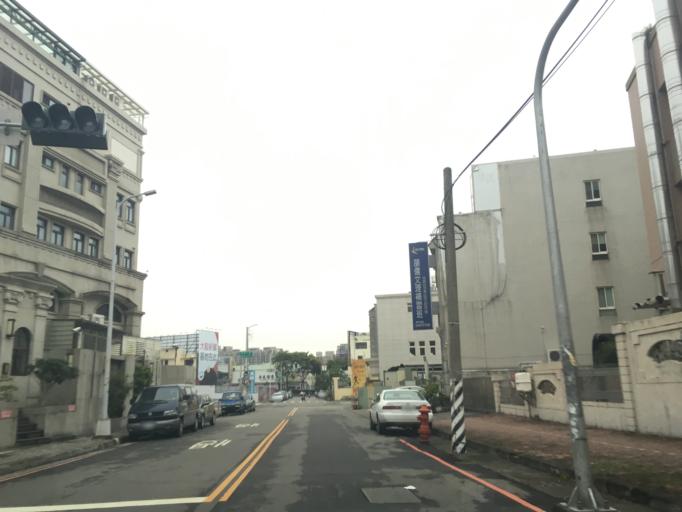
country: TW
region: Taiwan
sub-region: Taichung City
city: Taichung
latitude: 24.1660
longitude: 120.7136
